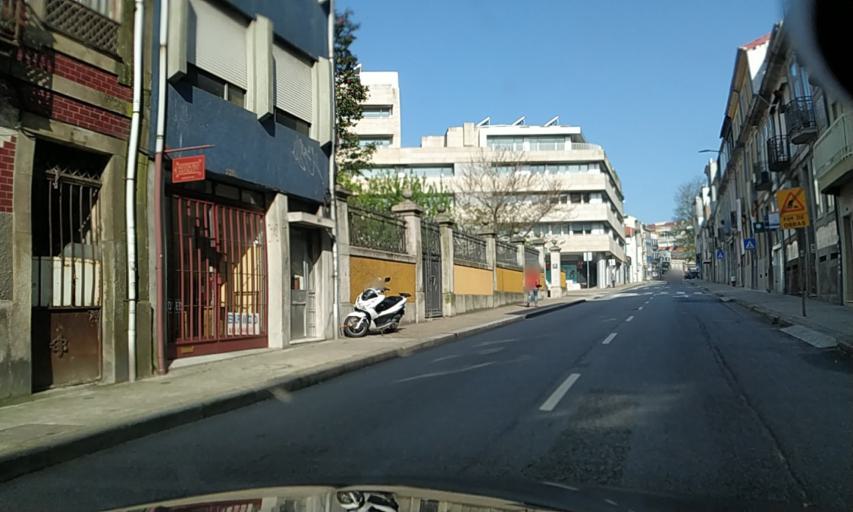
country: PT
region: Porto
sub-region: Porto
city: Porto
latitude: 41.1582
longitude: -8.6228
